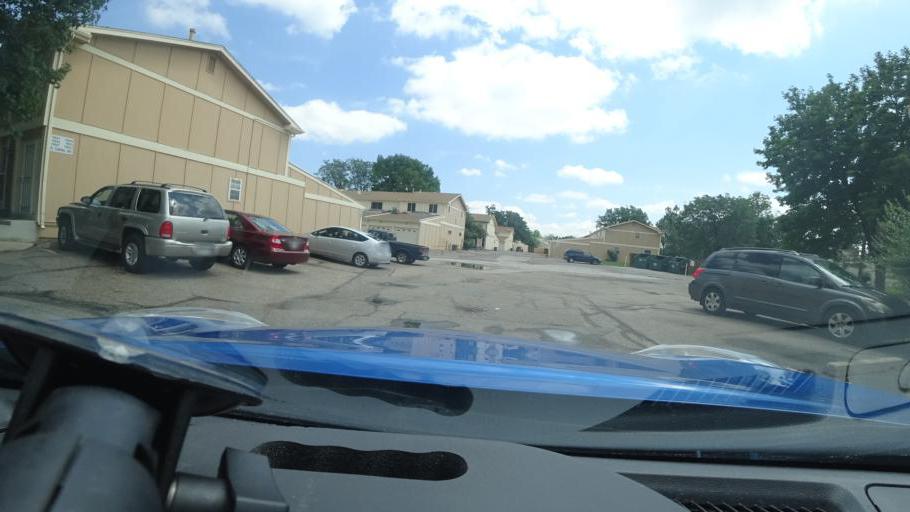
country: US
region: Colorado
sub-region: Adams County
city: Aurora
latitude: 39.7206
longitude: -104.8493
